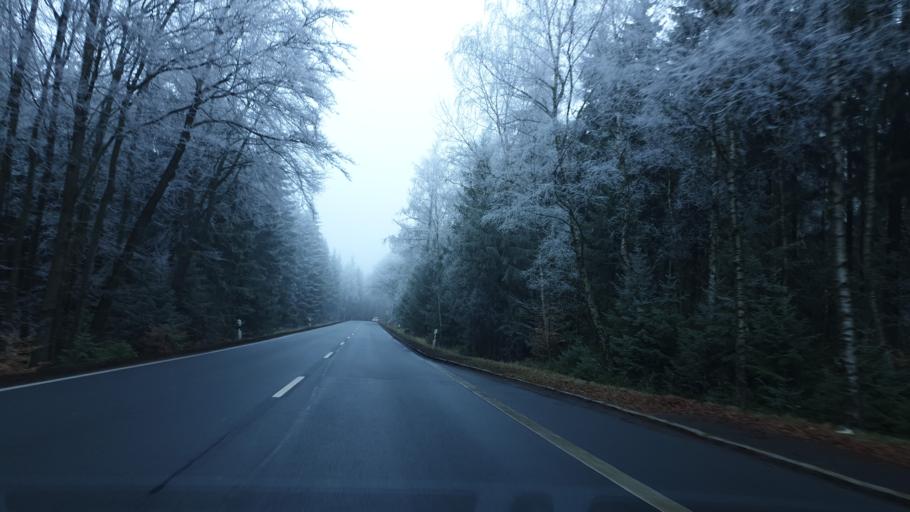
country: DE
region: Saxony
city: Bad Brambach
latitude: 50.1960
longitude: 12.3146
